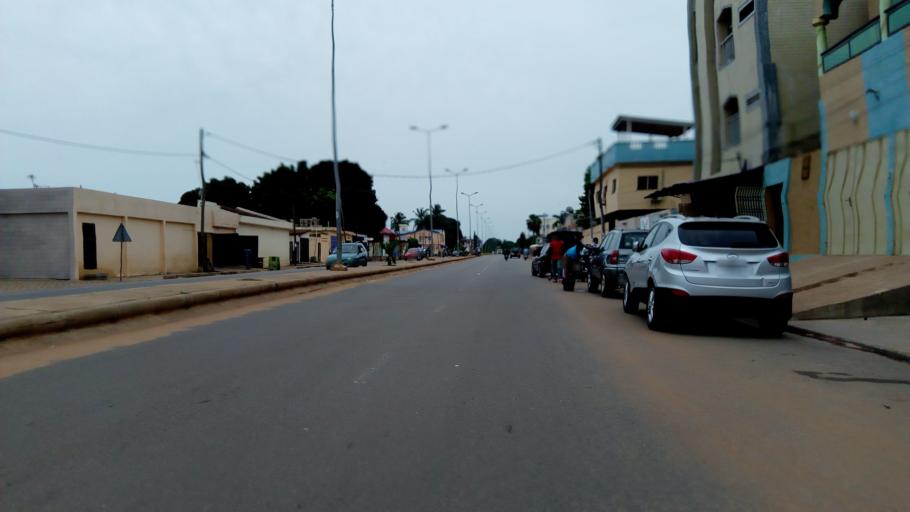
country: TG
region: Maritime
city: Lome
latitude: 6.1605
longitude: 1.2298
